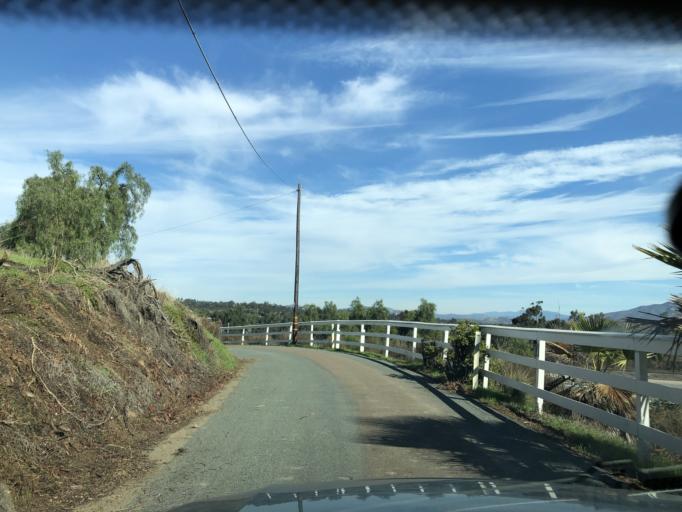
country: US
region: California
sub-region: San Diego County
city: Chula Vista
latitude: 32.6445
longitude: -117.0601
